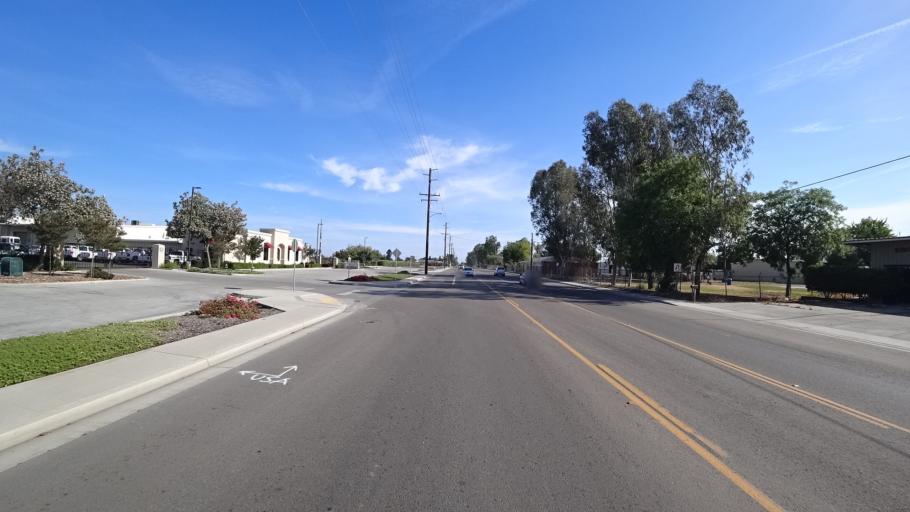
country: US
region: California
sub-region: Kings County
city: Home Garden
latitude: 36.3150
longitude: -119.6371
